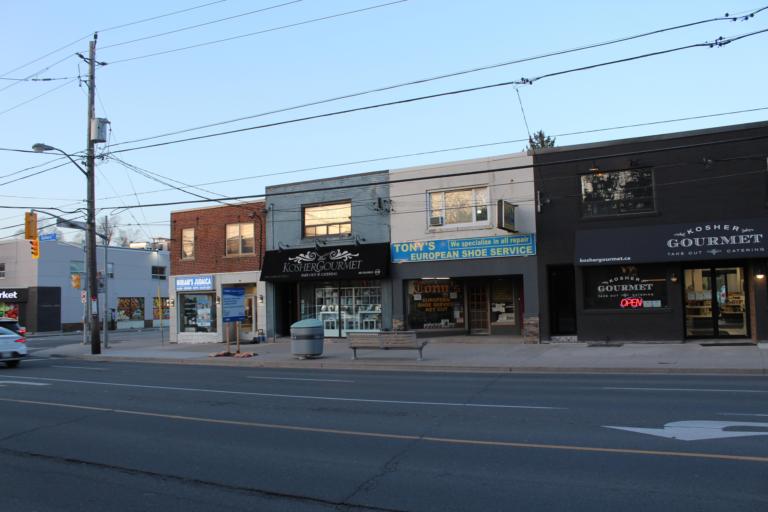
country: CA
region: Ontario
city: Toronto
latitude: 43.7172
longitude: -79.4294
